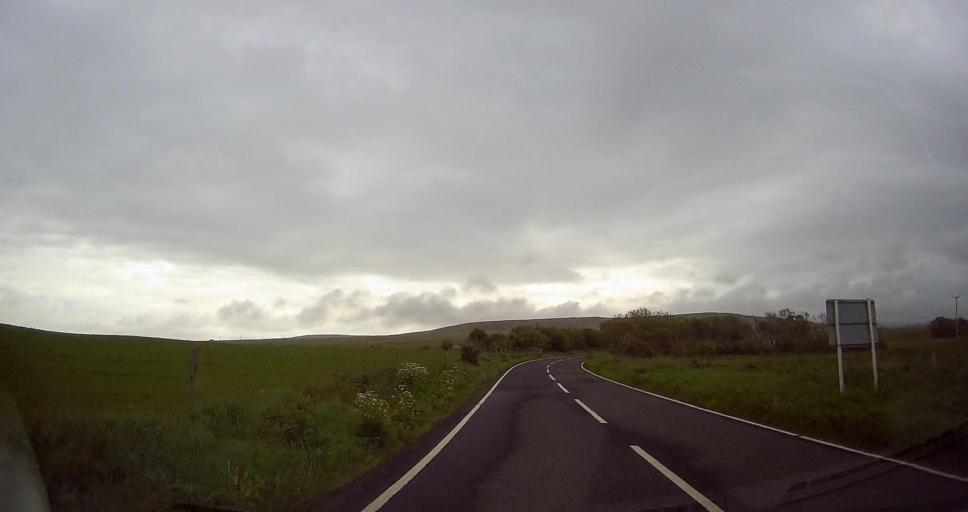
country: GB
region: Scotland
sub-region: Orkney Islands
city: Stromness
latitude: 59.0973
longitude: -3.2730
